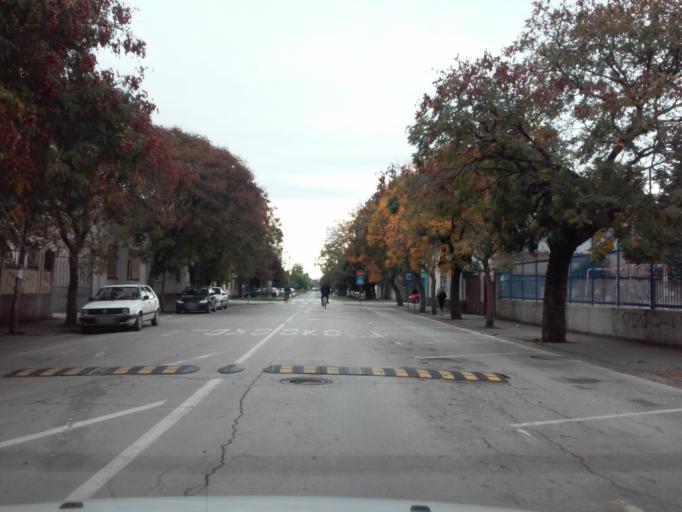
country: RS
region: Autonomna Pokrajina Vojvodina
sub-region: Severnobanatski Okrug
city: Kikinda
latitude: 45.8294
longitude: 20.4693
